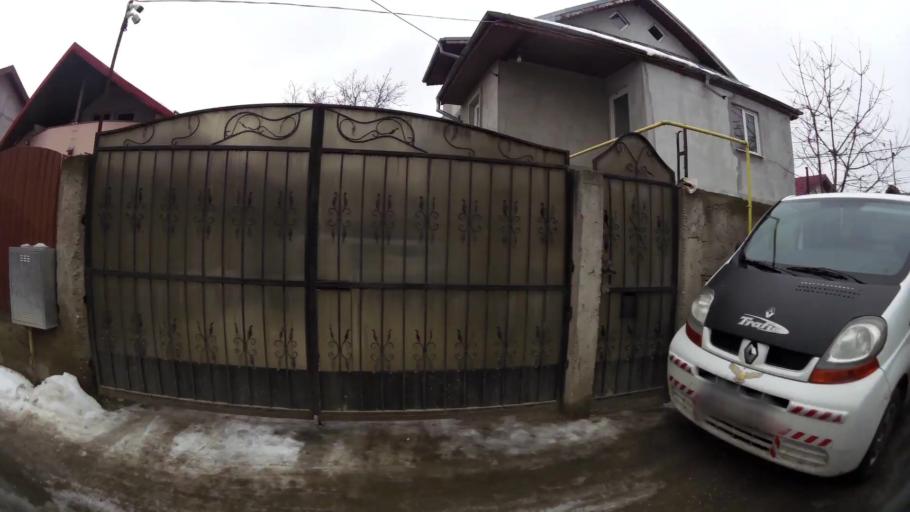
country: RO
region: Ilfov
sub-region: Comuna Pantelimon
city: Pantelimon
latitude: 44.4576
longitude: 26.1993
